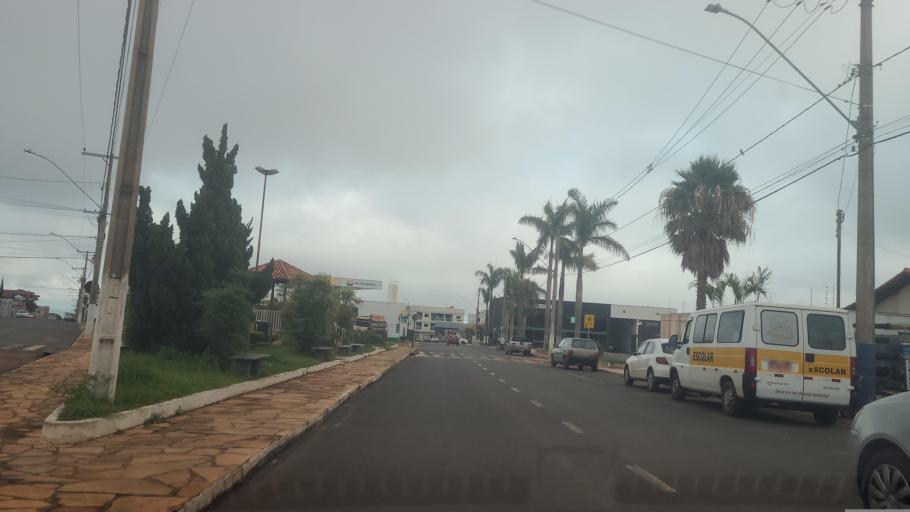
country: BR
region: Minas Gerais
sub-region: Carmo Do Paranaiba
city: Carmo do Paranaiba
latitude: -19.1985
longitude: -46.2365
